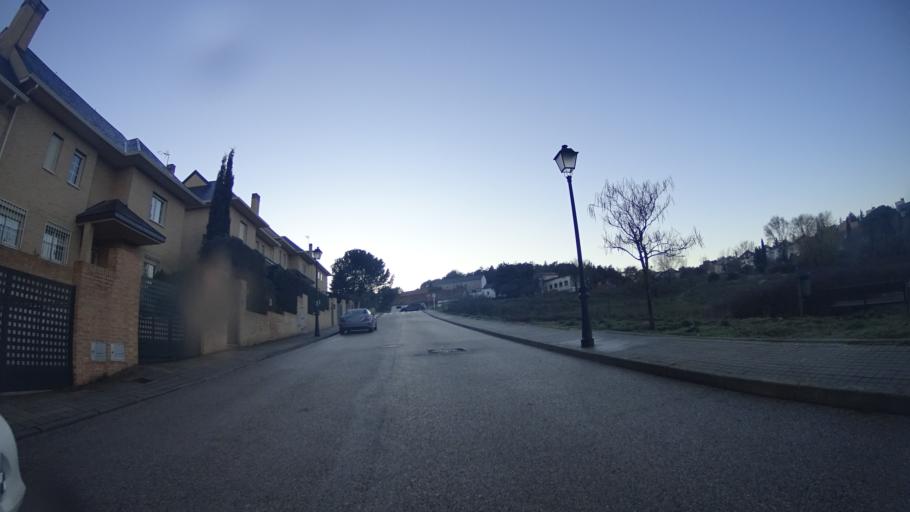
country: ES
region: Madrid
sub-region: Provincia de Madrid
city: Torrelodones
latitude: 40.5767
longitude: -3.9172
